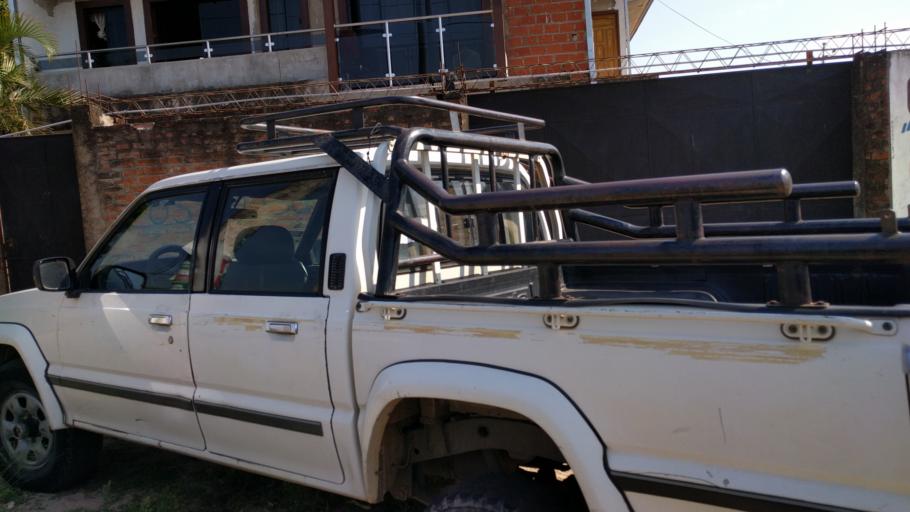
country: BO
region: Santa Cruz
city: Santa Cruz de la Sierra
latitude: -17.8159
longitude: -63.1706
